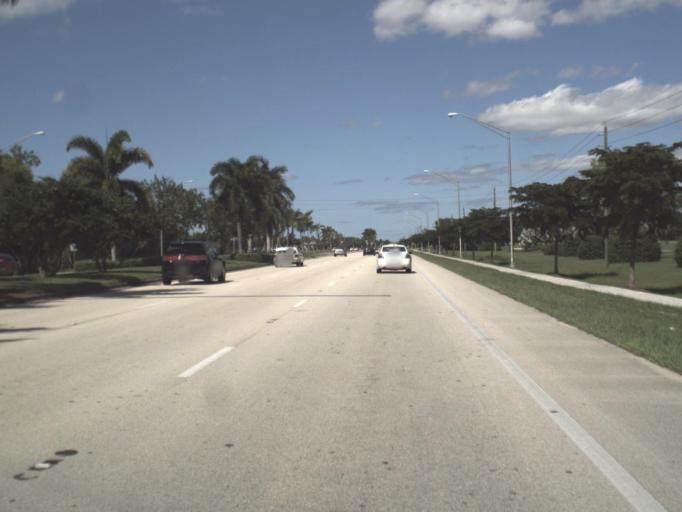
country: US
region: Florida
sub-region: Collier County
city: Lely
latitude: 26.1004
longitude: -81.7416
